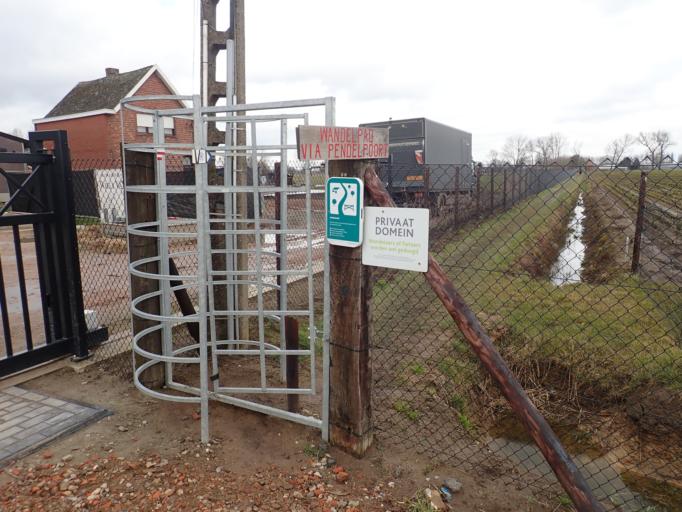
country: BE
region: Flanders
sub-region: Provincie Antwerpen
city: Lier
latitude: 51.1021
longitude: 4.5703
